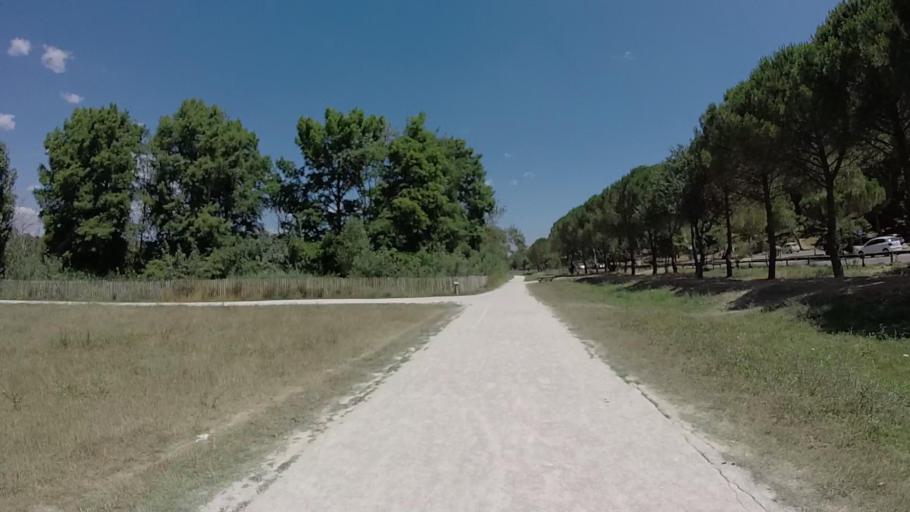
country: FR
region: Provence-Alpes-Cote d'Azur
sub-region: Departement des Alpes-Maritimes
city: Mougins
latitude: 43.5968
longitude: 7.0120
